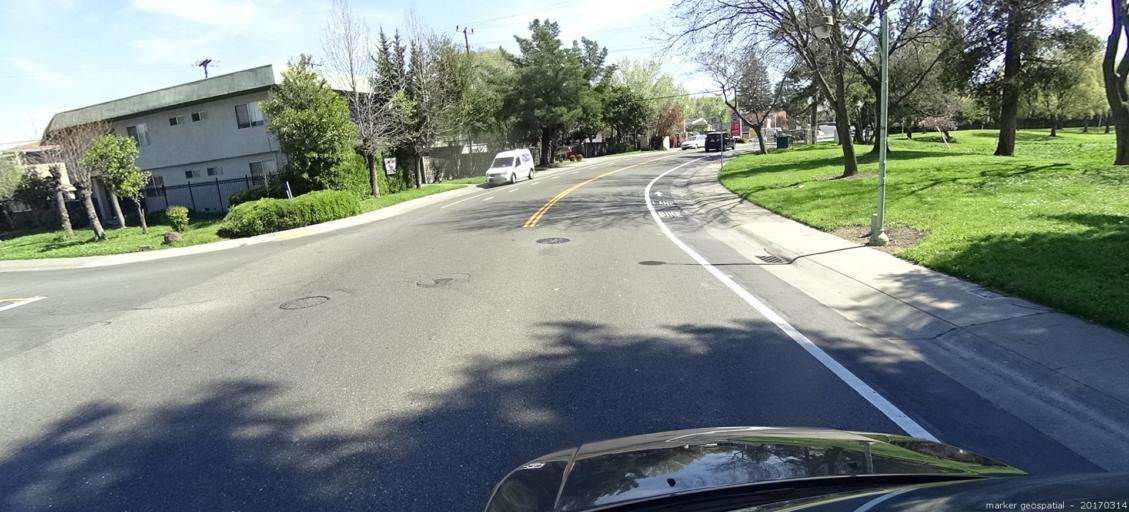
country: US
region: California
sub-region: Sacramento County
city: Parkway
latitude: 38.5168
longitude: -121.5170
